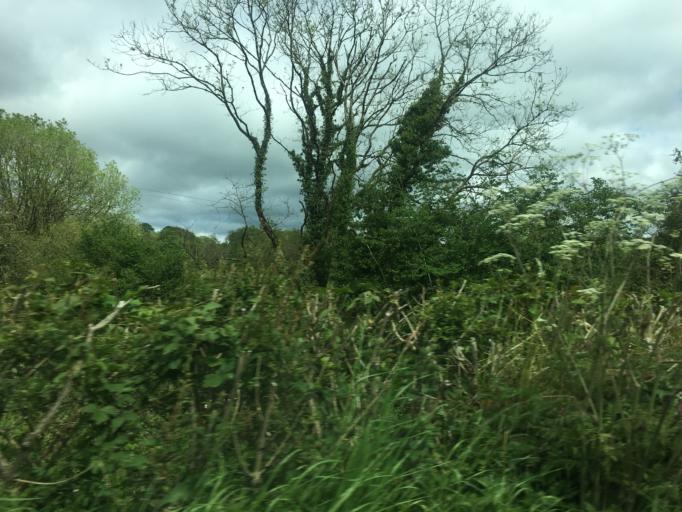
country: GB
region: Wales
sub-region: Carmarthenshire
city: Llansawel
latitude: 52.0712
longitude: -3.9903
